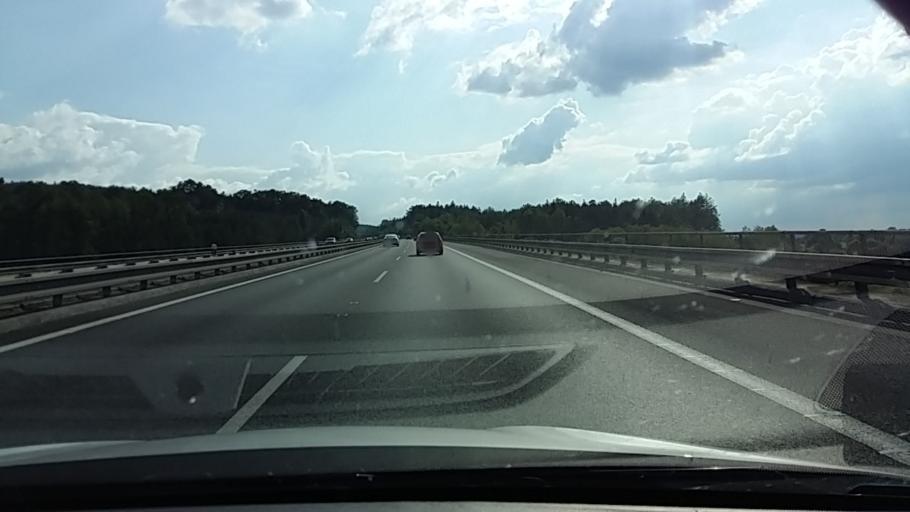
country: CZ
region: Plzensky
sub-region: Okres Rokycany
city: Rokycany
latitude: 49.7491
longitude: 13.5595
